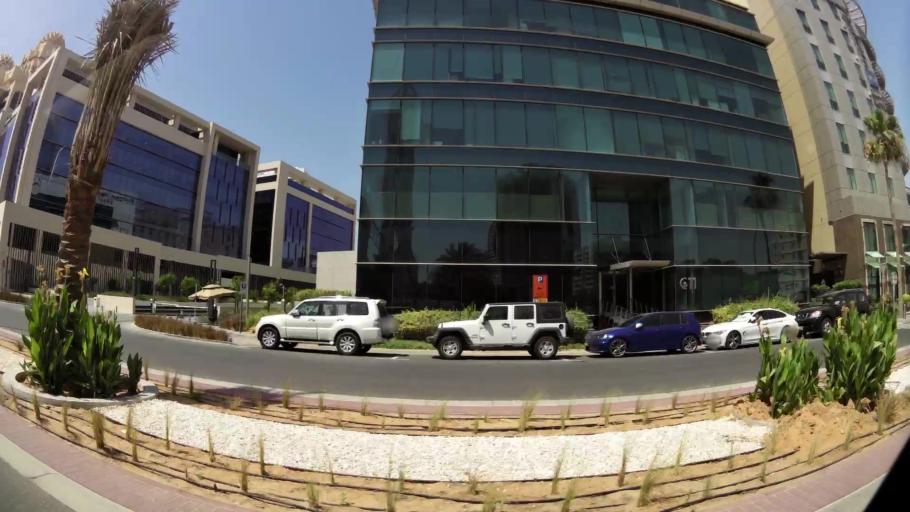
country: AE
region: Dubai
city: Dubai
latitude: 25.0936
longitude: 55.1549
